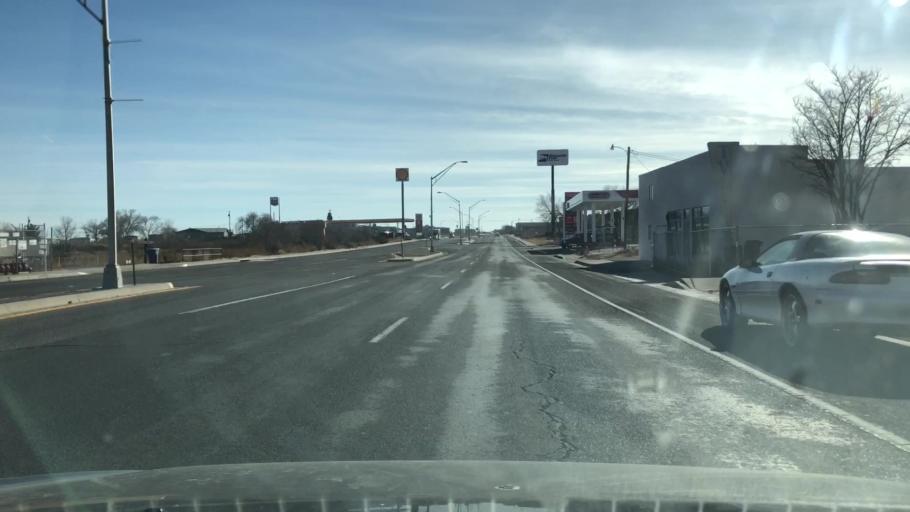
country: US
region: New Mexico
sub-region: Socorro County
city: Socorro
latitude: 34.0500
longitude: -106.8919
